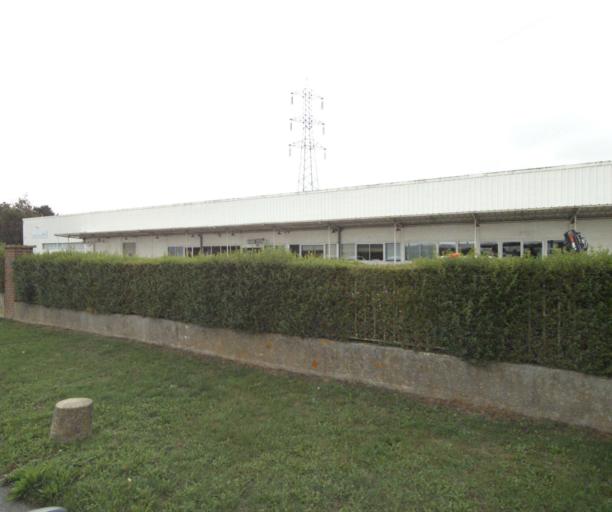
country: FR
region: Nord-Pas-de-Calais
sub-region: Departement du Nord
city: Lezennes
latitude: 50.6197
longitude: 3.1096
